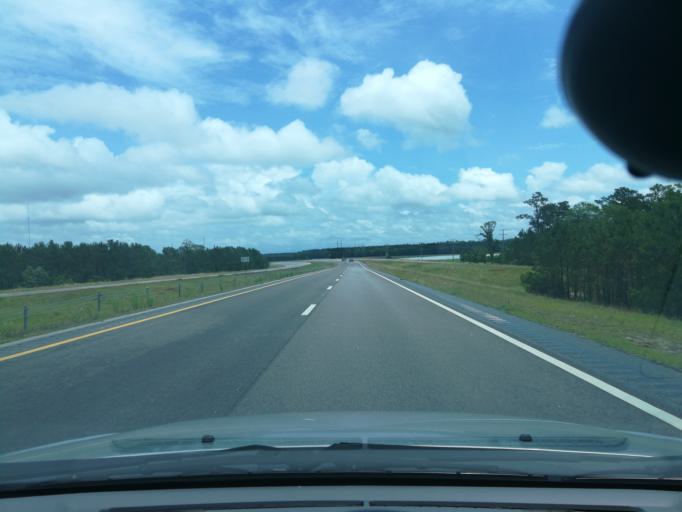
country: US
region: North Carolina
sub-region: Tyrrell County
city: Columbia
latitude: 35.8751
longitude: -76.3877
